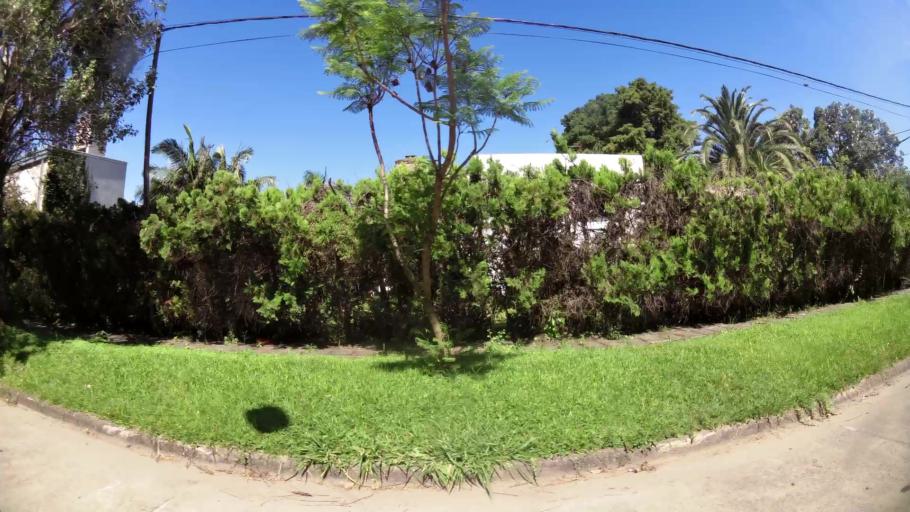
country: AR
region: Santa Fe
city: Santa Fe de la Vera Cruz
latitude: -31.6013
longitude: -60.6682
